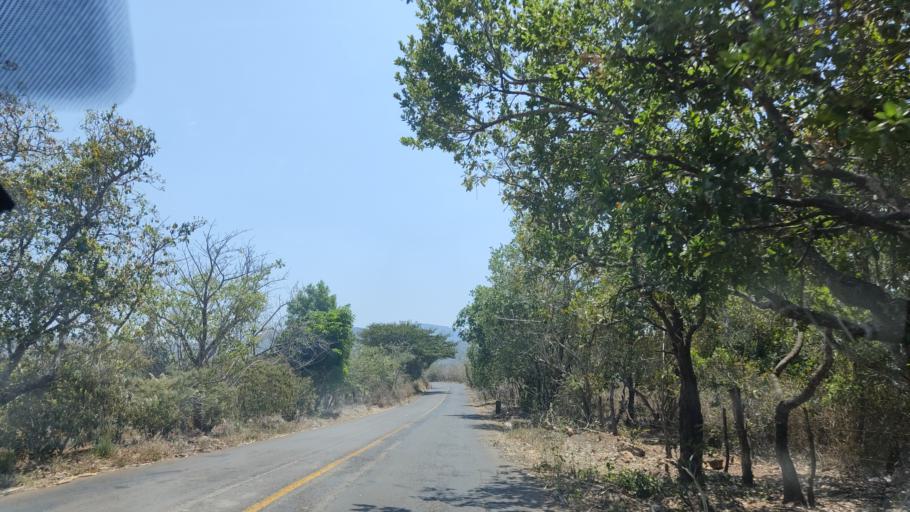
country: MX
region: Nayarit
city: Puga
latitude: 21.5817
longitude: -104.7754
